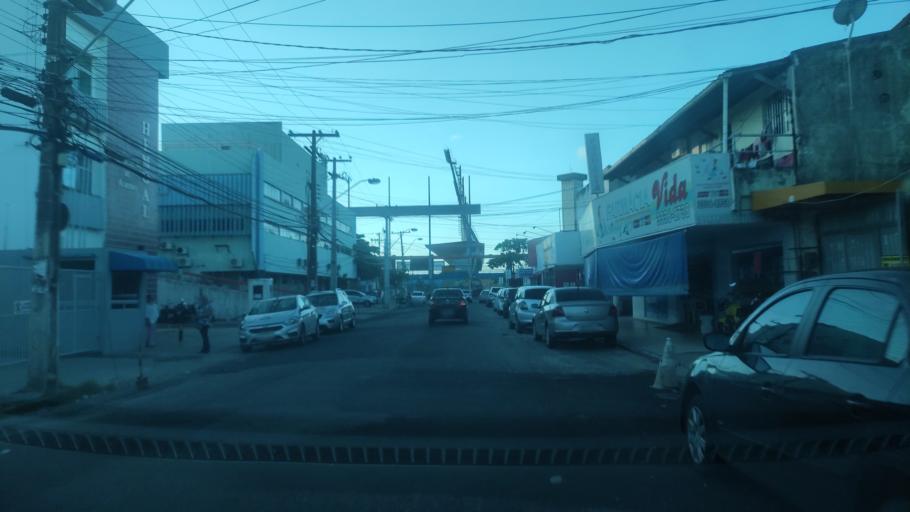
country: BR
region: Alagoas
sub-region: Maceio
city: Maceio
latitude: -9.6728
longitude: -35.7582
